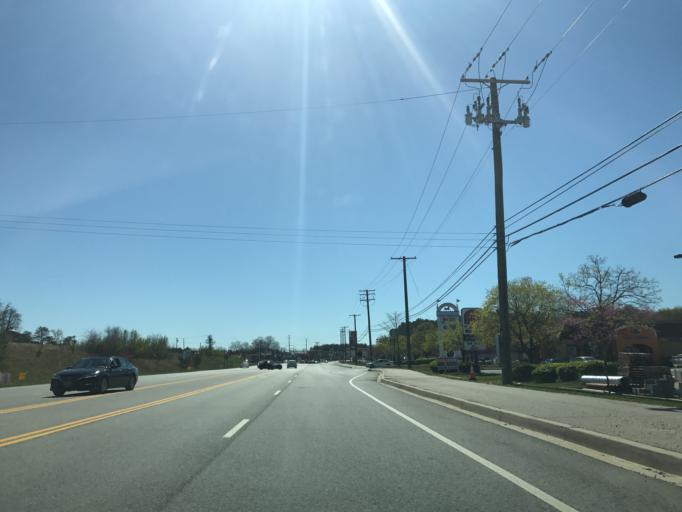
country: US
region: Maryland
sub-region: Anne Arundel County
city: Fort Meade
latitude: 39.1323
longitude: -76.7413
